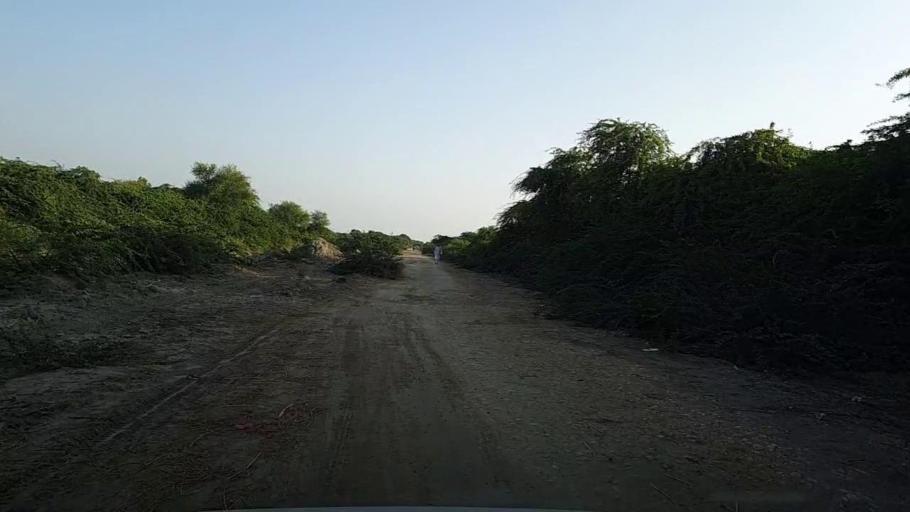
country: PK
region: Sindh
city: Kario
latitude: 24.7199
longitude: 68.6673
